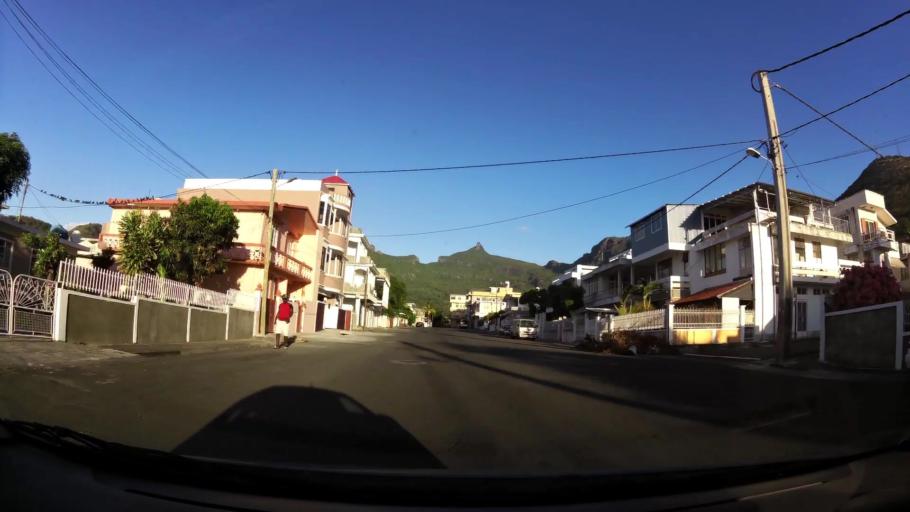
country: MU
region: Port Louis
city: Port Louis
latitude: -20.1737
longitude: 57.5063
